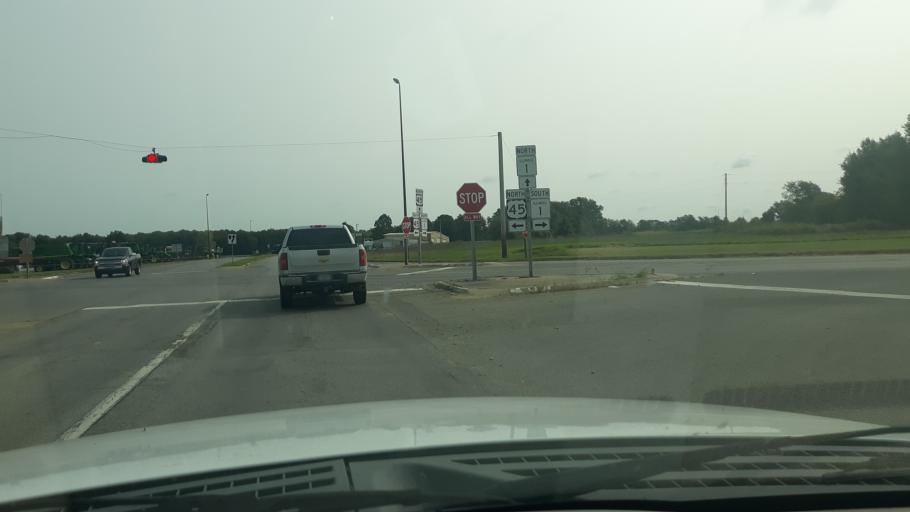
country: US
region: Illinois
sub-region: White County
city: Norris City
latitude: 37.9656
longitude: -88.3284
